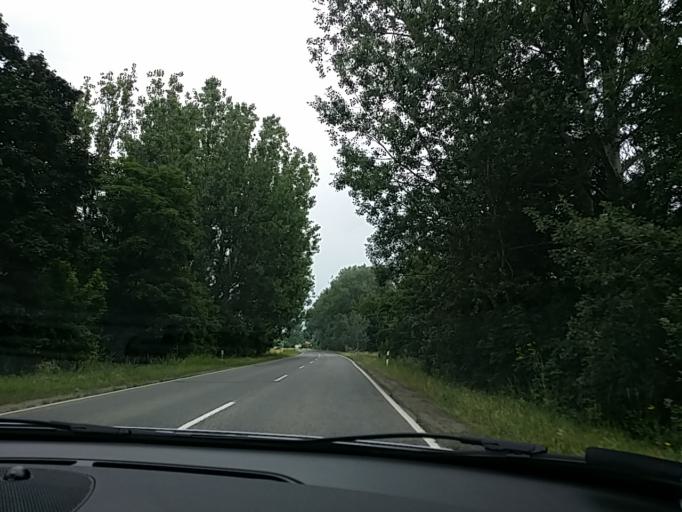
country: HU
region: Nograd
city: Batonyterenye
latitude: 48.0004
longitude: 19.8223
